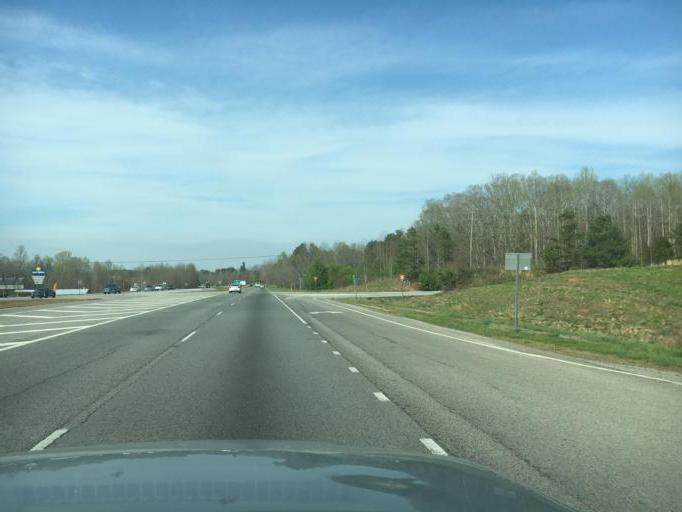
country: US
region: Georgia
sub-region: Banks County
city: Alto
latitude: 34.4862
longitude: -83.5827
